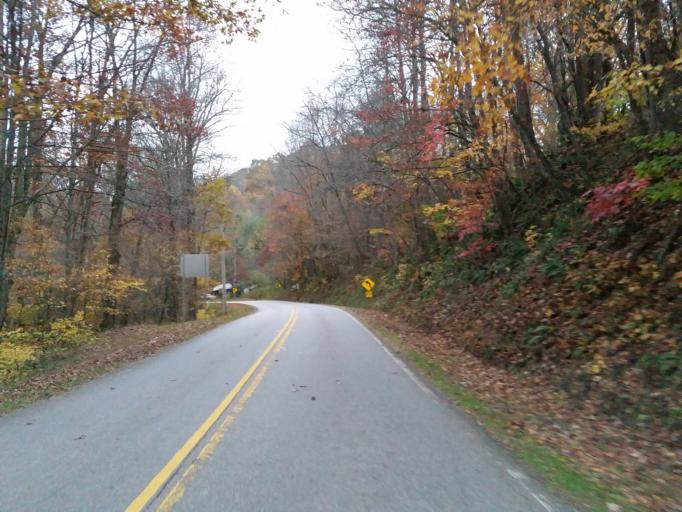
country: US
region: Georgia
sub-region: Lumpkin County
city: Dahlonega
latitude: 34.7035
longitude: -84.0554
